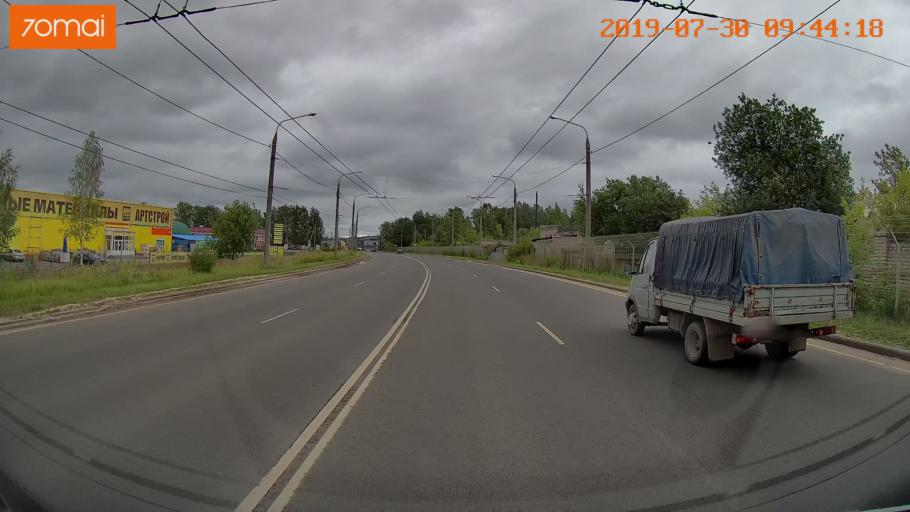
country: RU
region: Ivanovo
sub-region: Gorod Ivanovo
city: Ivanovo
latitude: 56.9486
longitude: 40.9617
